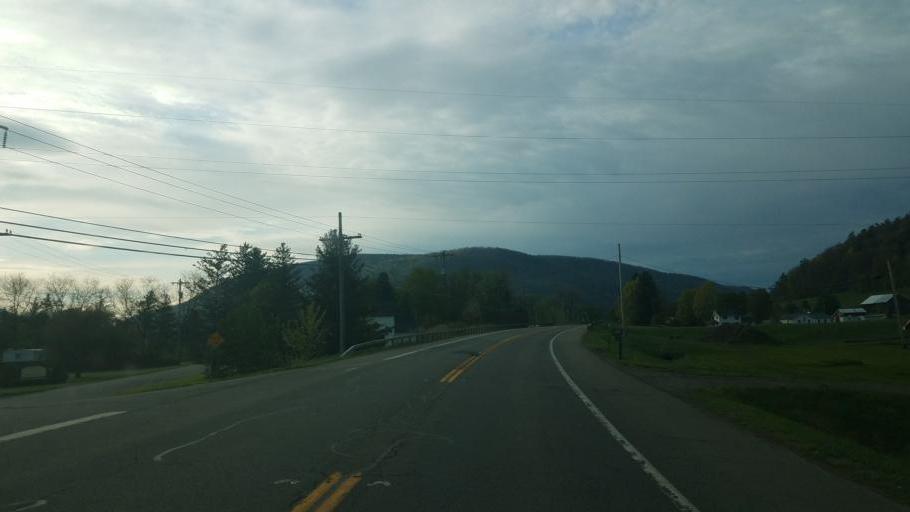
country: US
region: New York
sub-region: Steuben County
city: Canisteo
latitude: 42.2667
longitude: -77.5955
